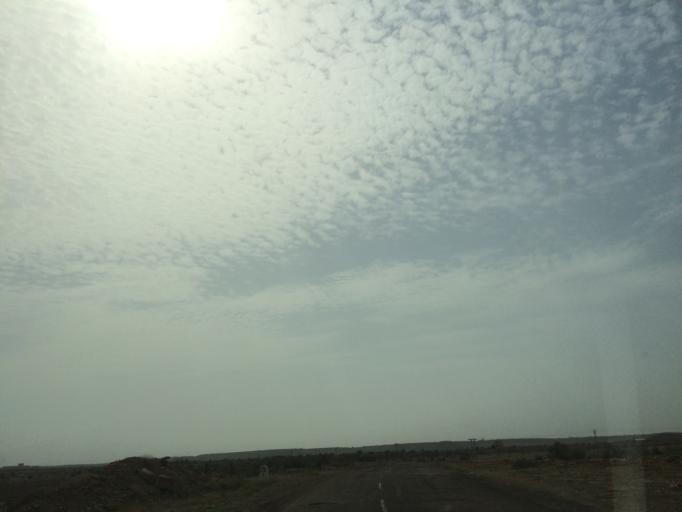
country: IN
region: Rajasthan
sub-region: Jaisalmer
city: Jaisalmer
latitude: 26.8744
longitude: 70.8708
